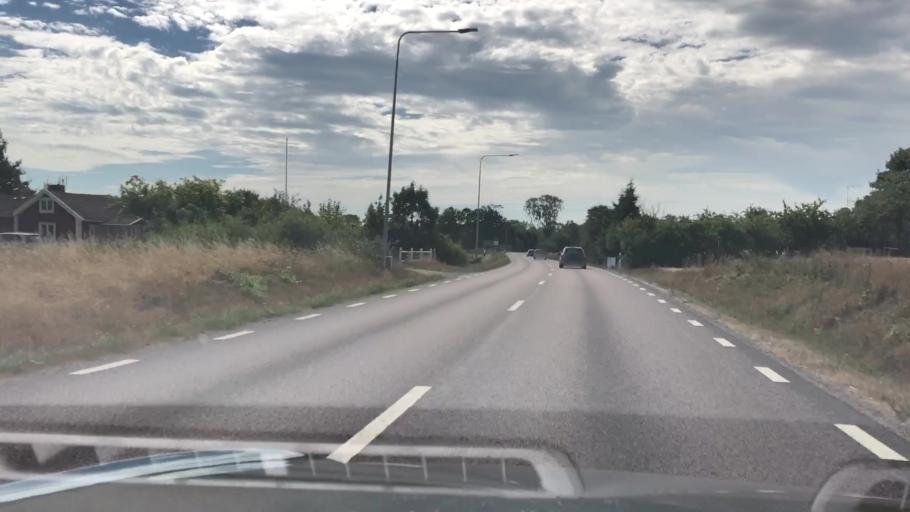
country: SE
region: Kalmar
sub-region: Torsas Kommun
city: Torsas
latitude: 56.3751
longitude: 16.0687
